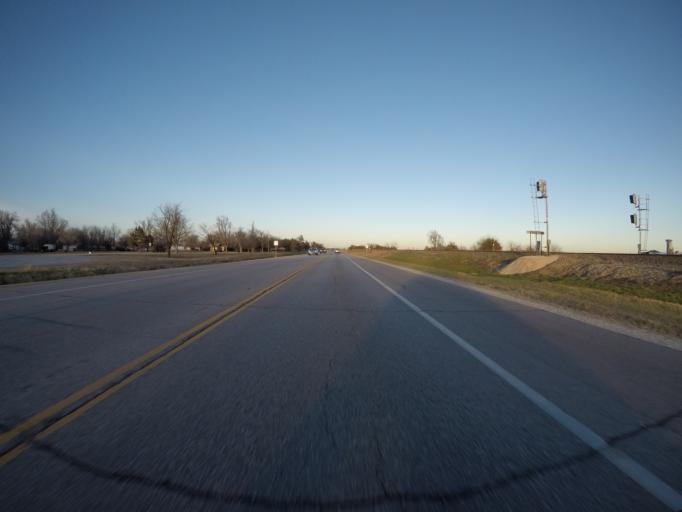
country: US
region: Kansas
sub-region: Harvey County
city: North Newton
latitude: 38.1188
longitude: -97.2546
